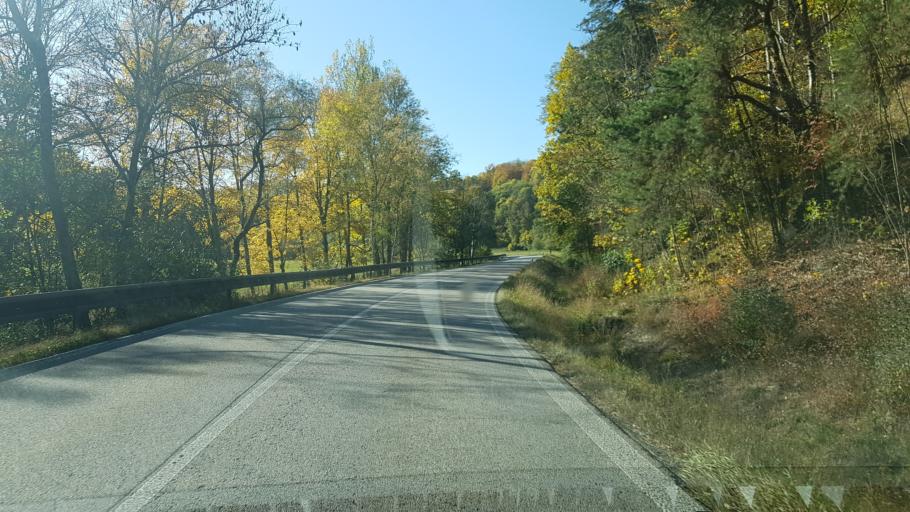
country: CZ
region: Jihocesky
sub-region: Okres Prachatice
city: Vimperk
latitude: 49.0866
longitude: 13.7923
